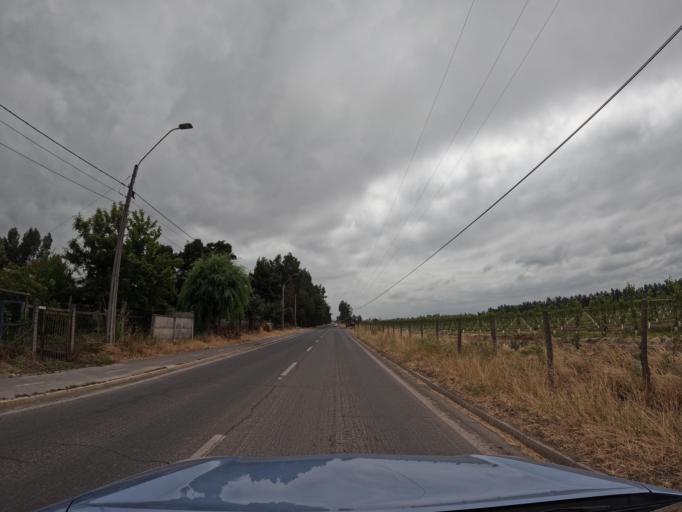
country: CL
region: O'Higgins
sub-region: Provincia de Colchagua
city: Chimbarongo
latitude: -34.7220
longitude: -71.0534
